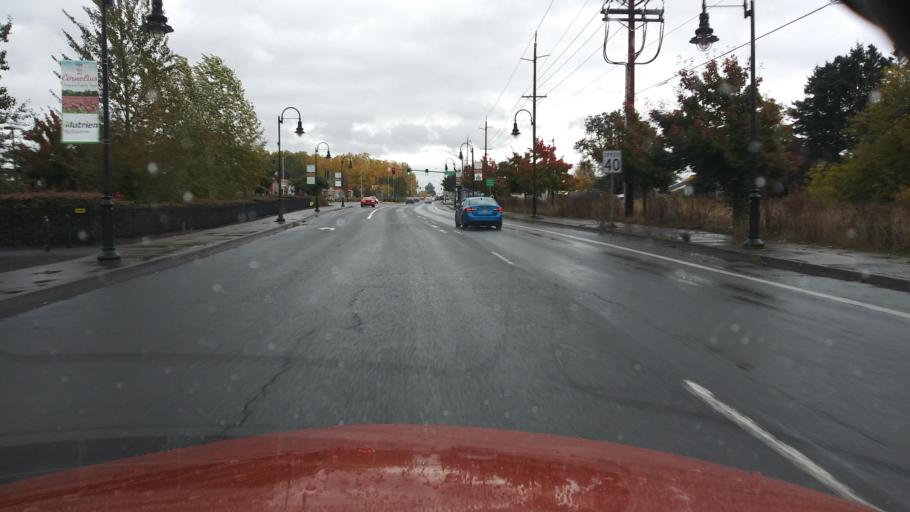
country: US
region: Oregon
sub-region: Washington County
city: Cornelius
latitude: 45.5201
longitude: -123.0487
